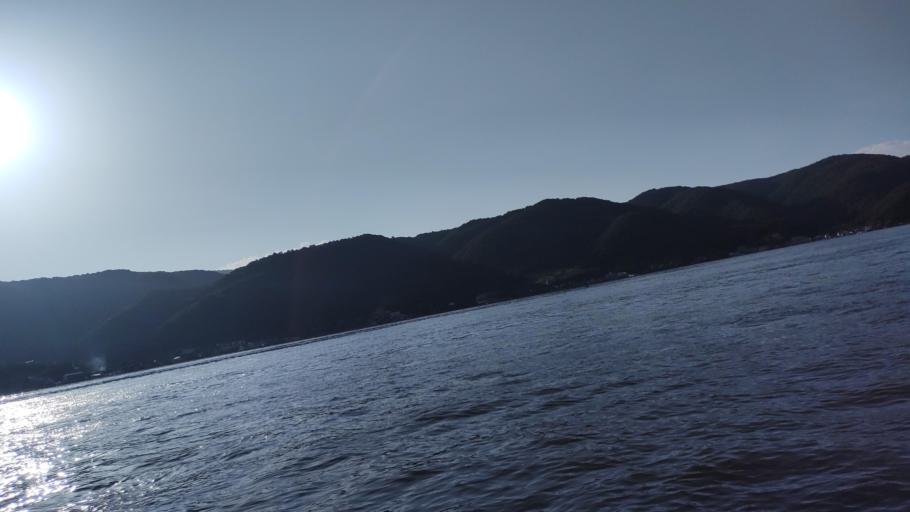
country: RO
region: Mehedinti
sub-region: Comuna Dubova
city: Dubova
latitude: 44.6183
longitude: 22.2732
